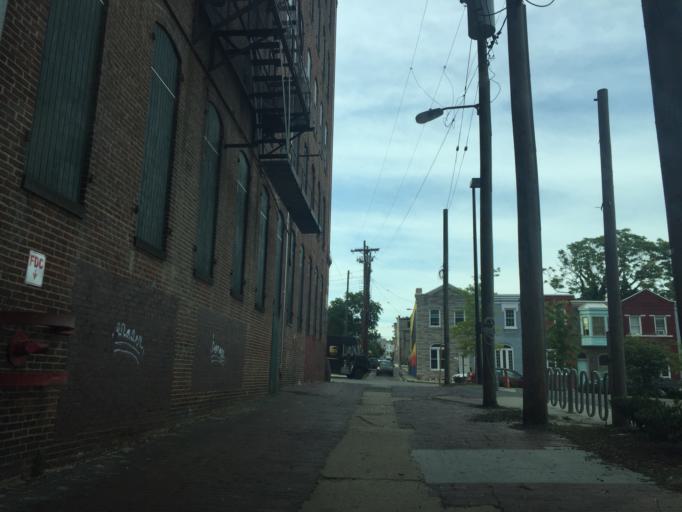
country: US
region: Maryland
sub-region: City of Baltimore
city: Baltimore
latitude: 39.3074
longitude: -76.6114
